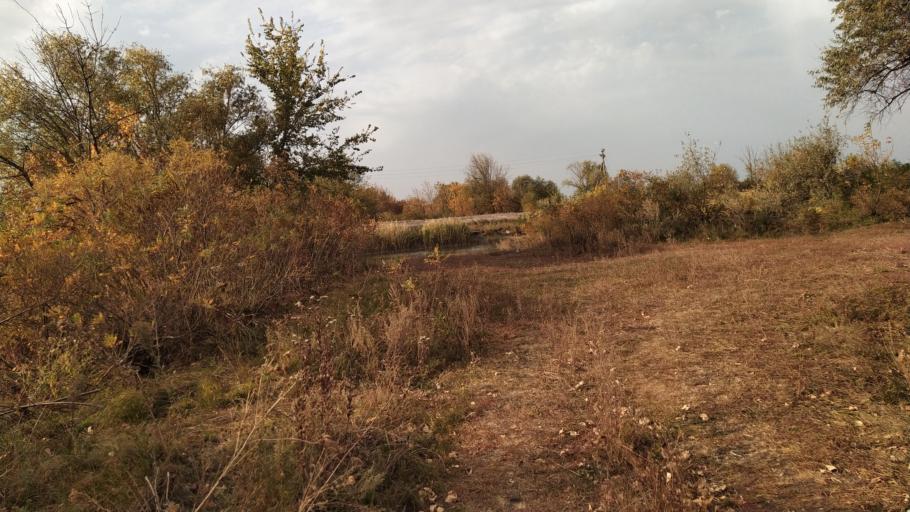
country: RU
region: Rostov
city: Kuleshovka
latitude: 47.1435
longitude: 39.5842
